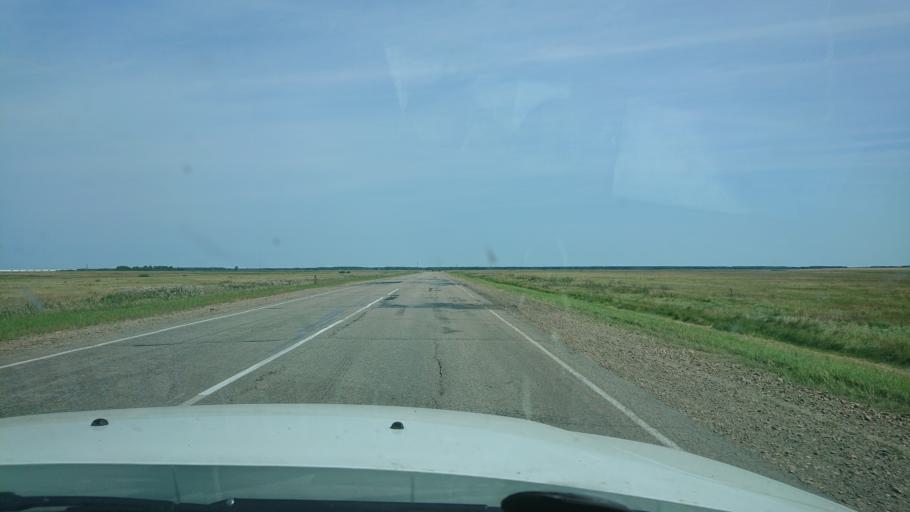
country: RU
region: Tjumen
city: Armizonskoye
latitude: 55.5378
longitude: 67.8999
